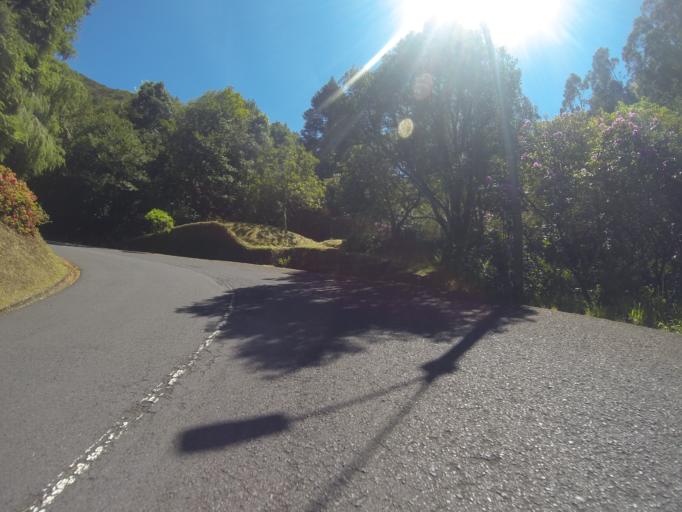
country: PT
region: Madeira
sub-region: Santana
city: Santana
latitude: 32.7338
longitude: -16.8875
